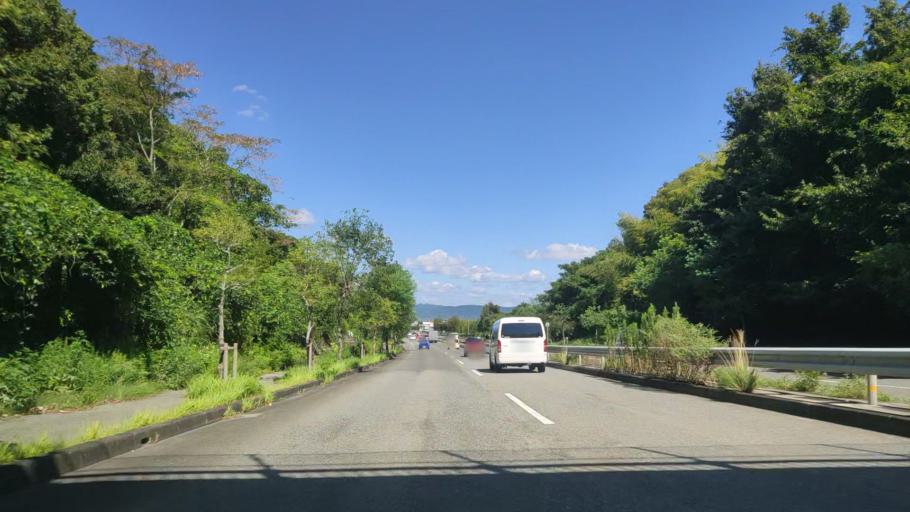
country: JP
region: Hyogo
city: Ono
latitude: 34.8750
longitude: 134.9519
